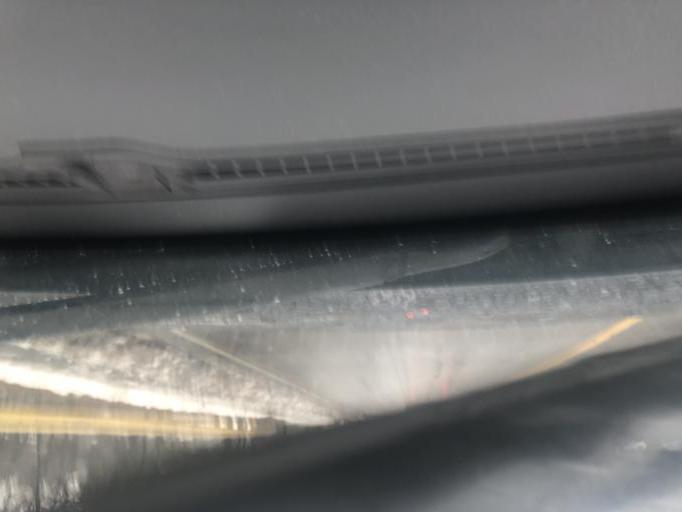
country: US
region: Massachusetts
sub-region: Norfolk County
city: Avon
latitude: 42.1015
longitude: -71.0437
